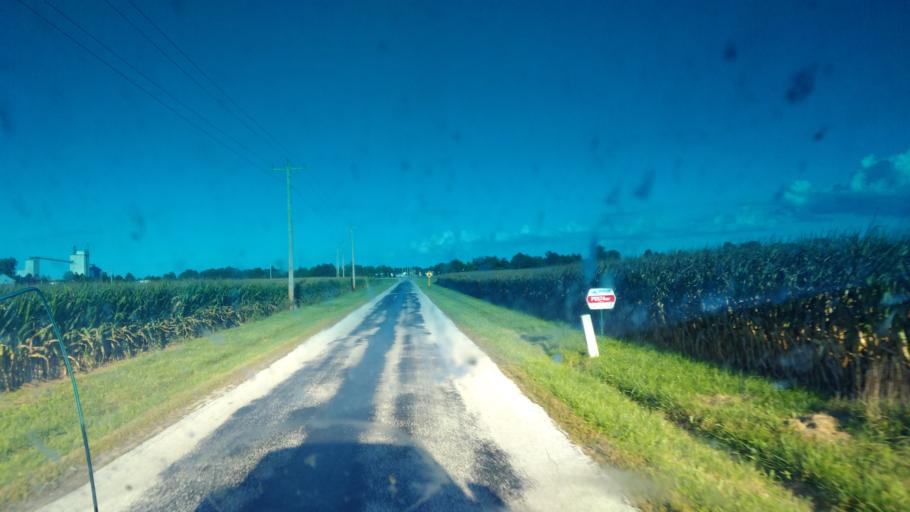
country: US
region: Ohio
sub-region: Wyandot County
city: Carey
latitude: 40.9015
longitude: -83.3499
